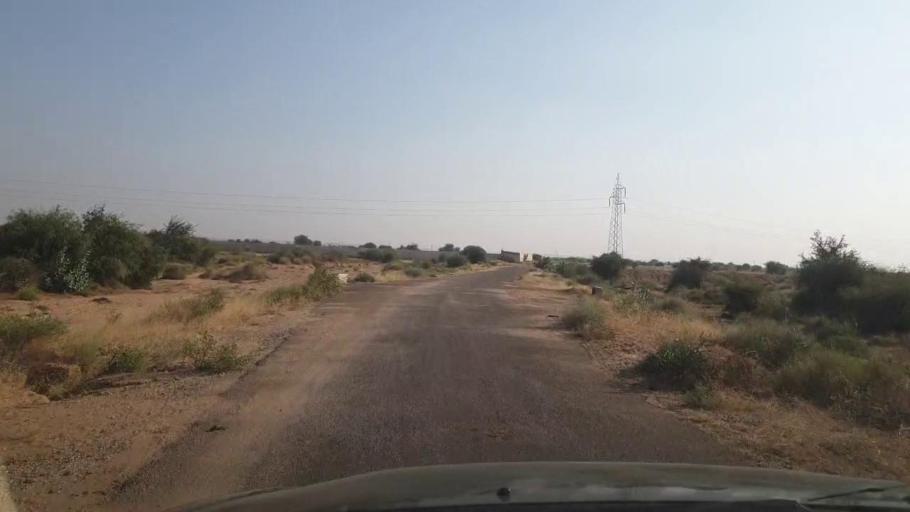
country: PK
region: Sindh
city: Jamshoro
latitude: 25.3509
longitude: 67.8373
